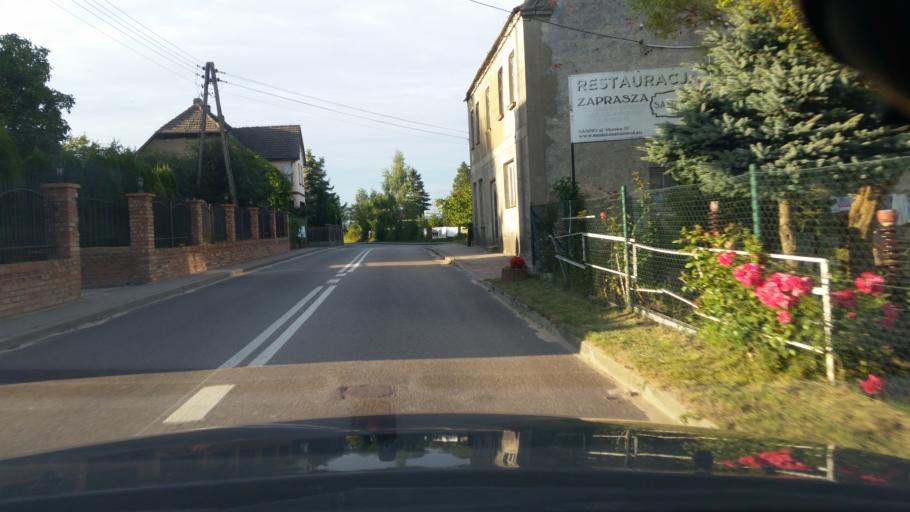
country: PL
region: Pomeranian Voivodeship
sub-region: Powiat wejherowski
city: Choczewo
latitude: 54.7591
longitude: 17.7520
